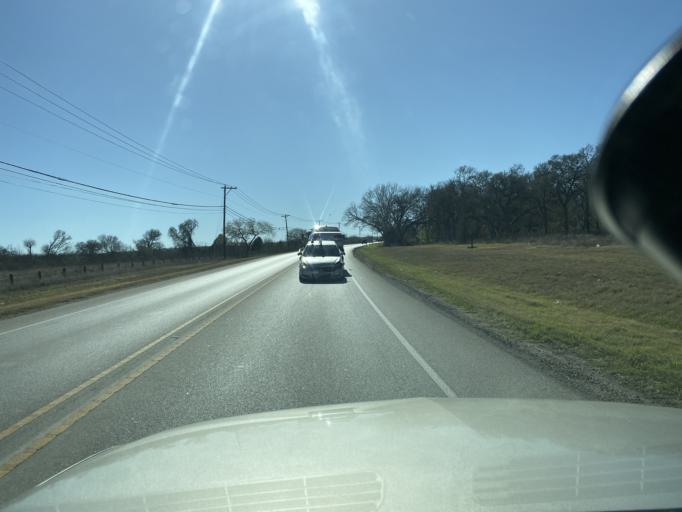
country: US
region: Texas
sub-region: Travis County
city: Garfield
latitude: 30.1790
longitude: -97.6473
